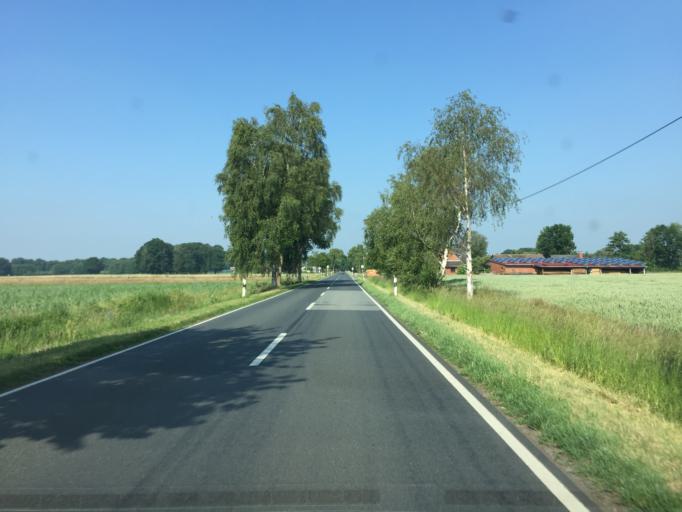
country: DE
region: Lower Saxony
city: Varrel
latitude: 52.5366
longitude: 8.7263
